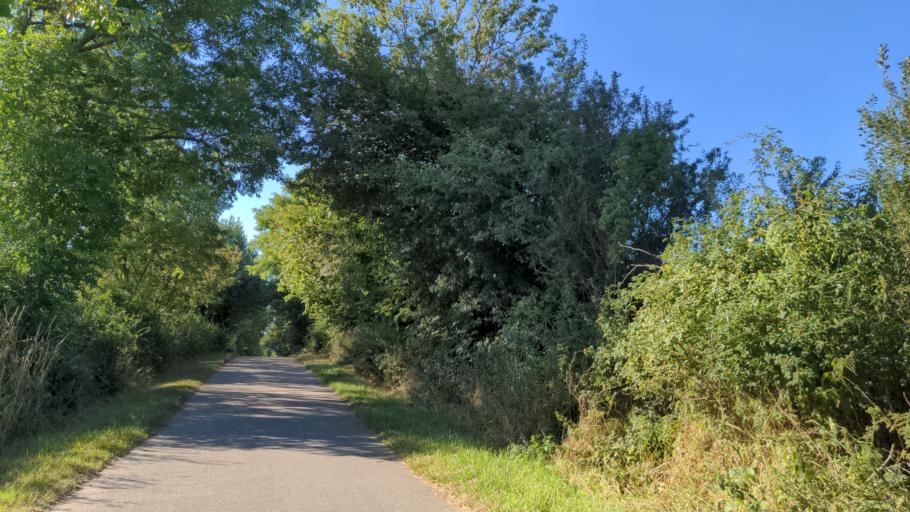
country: DE
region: Mecklenburg-Vorpommern
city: Ostseebad Boltenhagen
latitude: 54.0038
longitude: 11.1889
